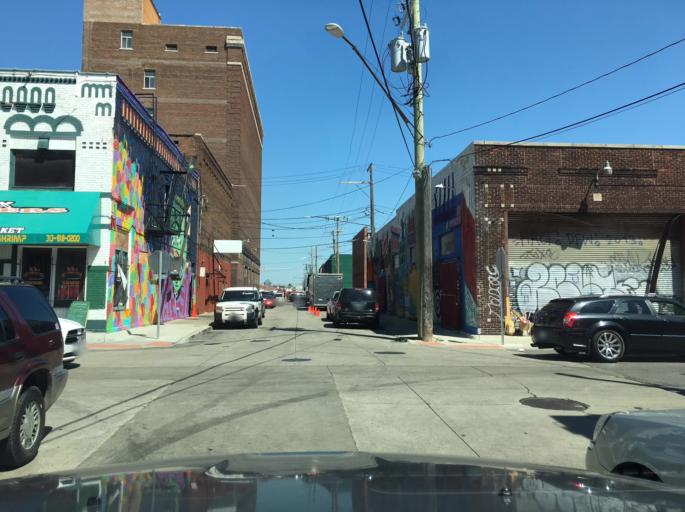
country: US
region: Michigan
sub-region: Wayne County
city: Detroit
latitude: 42.3464
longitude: -83.0385
